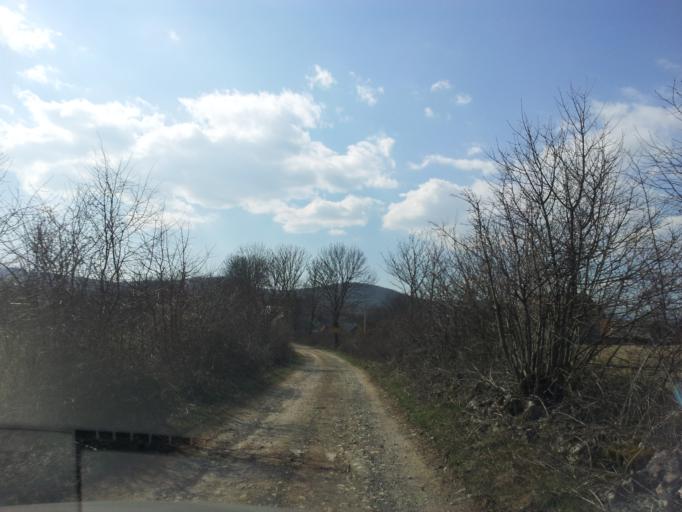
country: HR
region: Zadarska
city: Gracac
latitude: 44.5349
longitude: 15.7399
